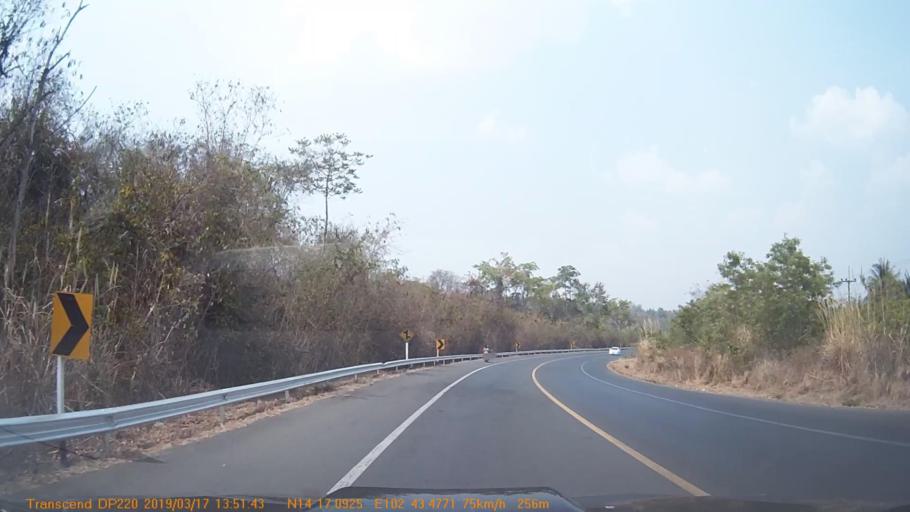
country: TH
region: Buriram
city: Non Din Daeng
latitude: 14.2852
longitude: 102.7246
